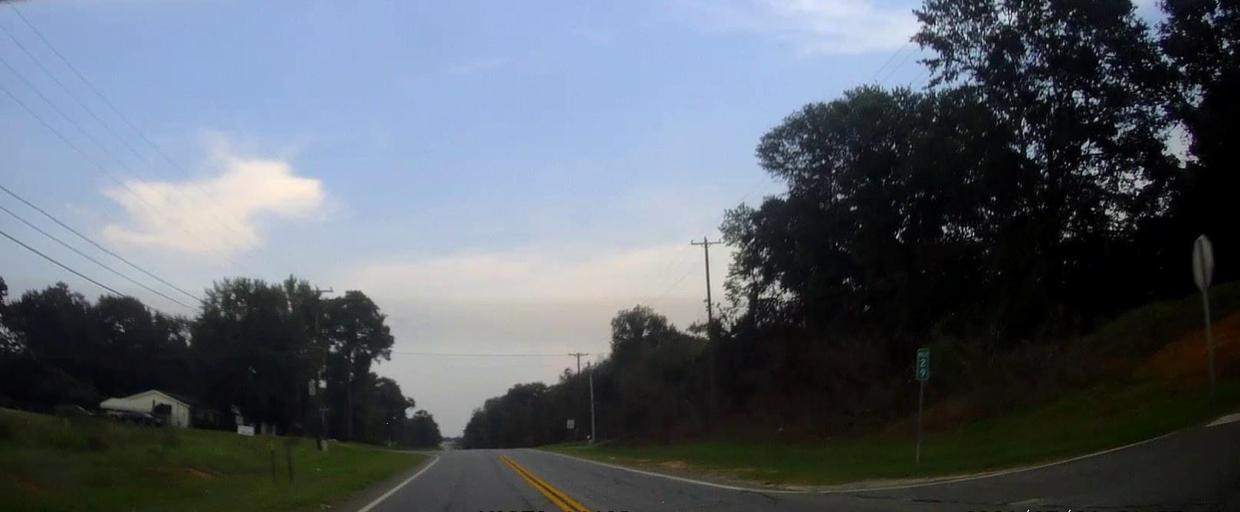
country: US
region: Georgia
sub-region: Laurens County
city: East Dublin
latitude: 32.5580
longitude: -82.8575
